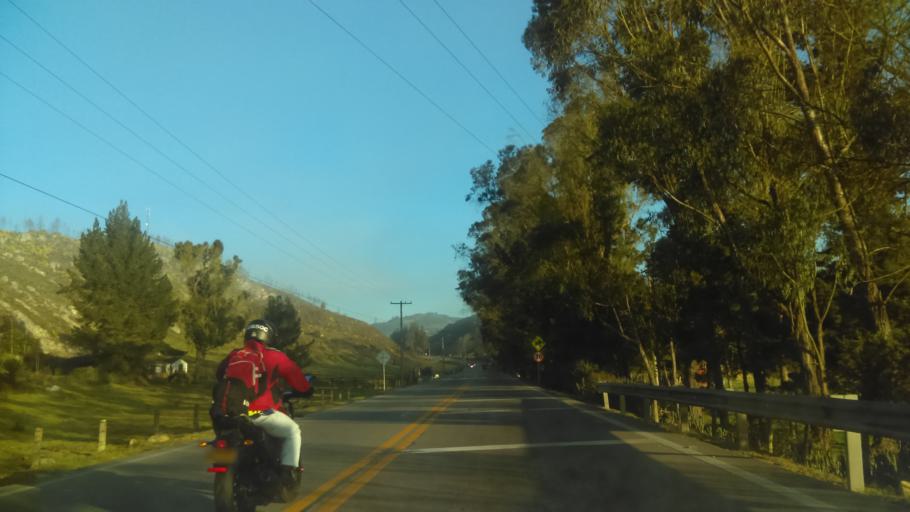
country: CO
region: Cundinamarca
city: San Antonio del Tequendama
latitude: 4.6175
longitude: -74.2826
